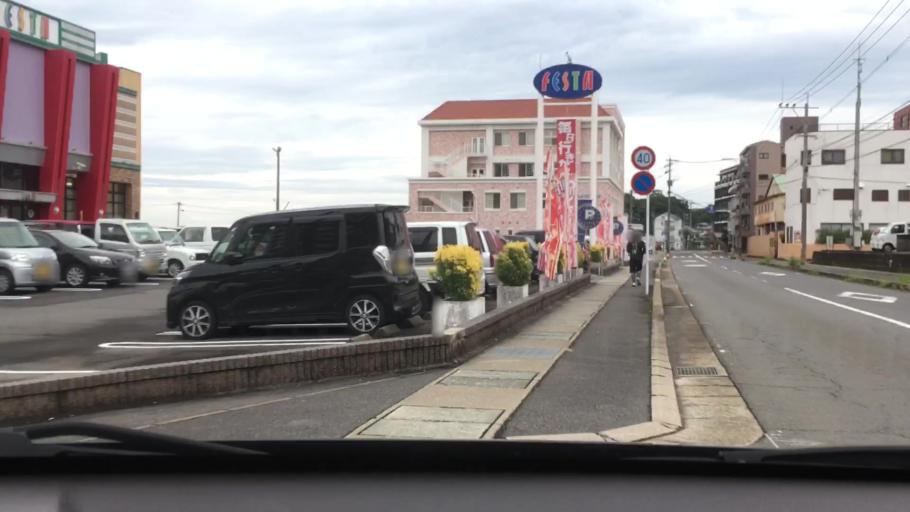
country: JP
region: Nagasaki
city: Nagasaki-shi
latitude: 32.7559
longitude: 129.9454
